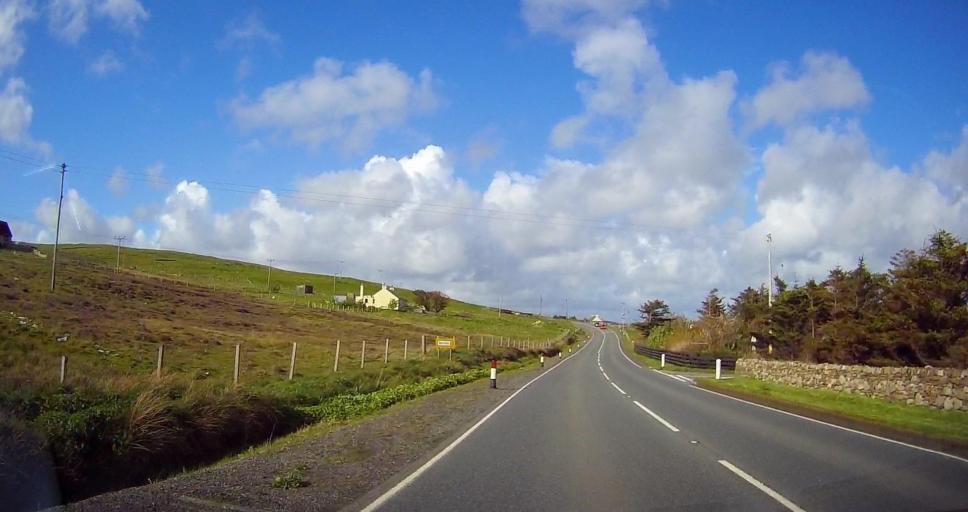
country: GB
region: Scotland
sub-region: Shetland Islands
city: Lerwick
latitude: 60.2354
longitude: -1.2326
